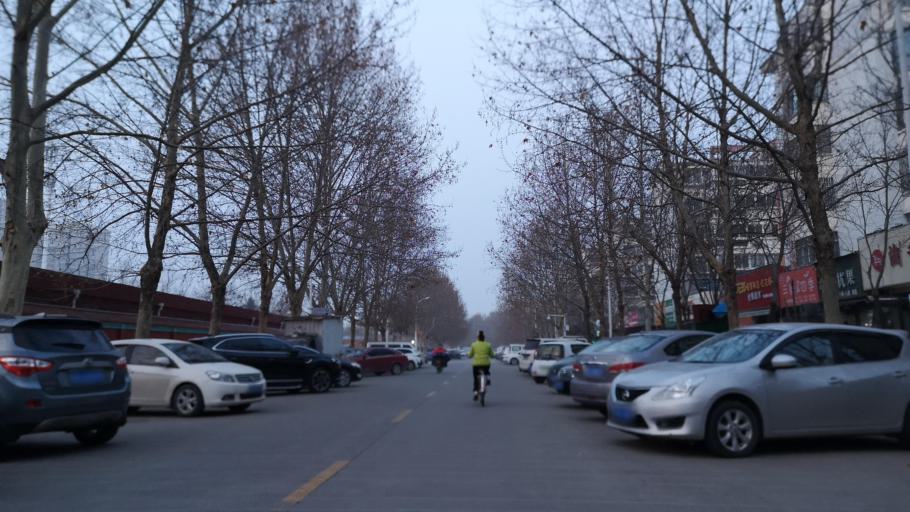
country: CN
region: Henan Sheng
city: Zhongyuanlu
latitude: 35.7551
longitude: 115.0611
